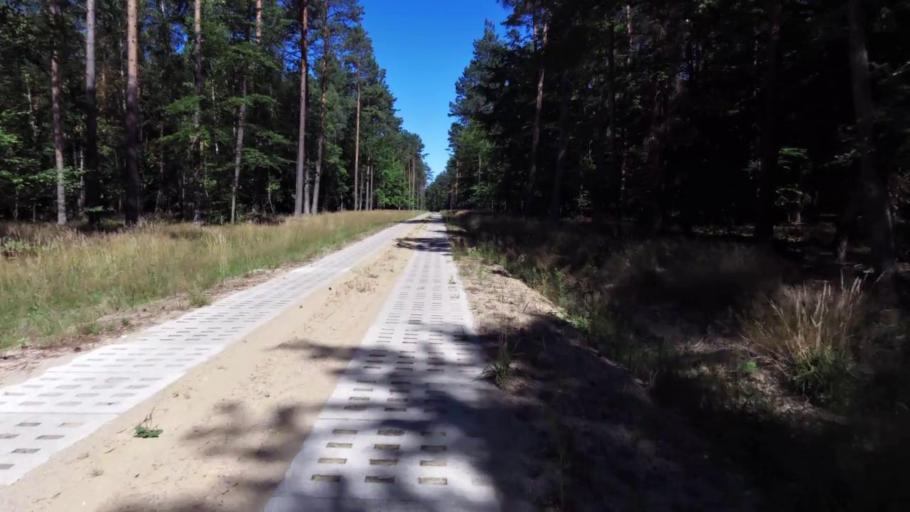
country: PL
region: West Pomeranian Voivodeship
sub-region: Powiat szczecinecki
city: Szczecinek
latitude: 53.6044
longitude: 16.6629
